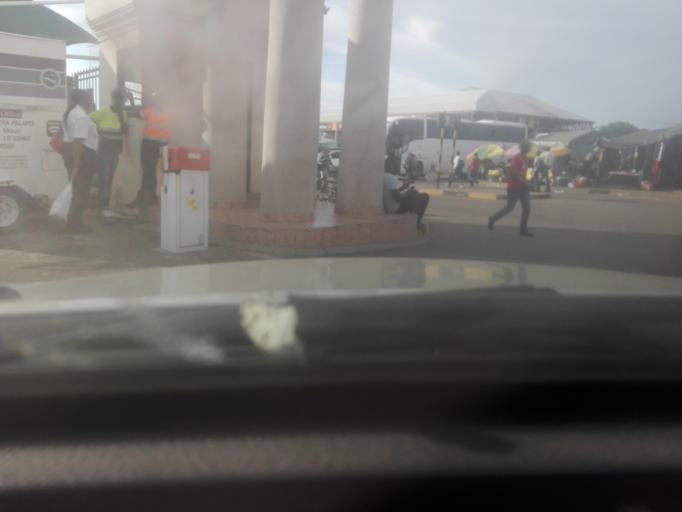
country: BW
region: South East
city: Gaborone
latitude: -24.6590
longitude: 25.9039
